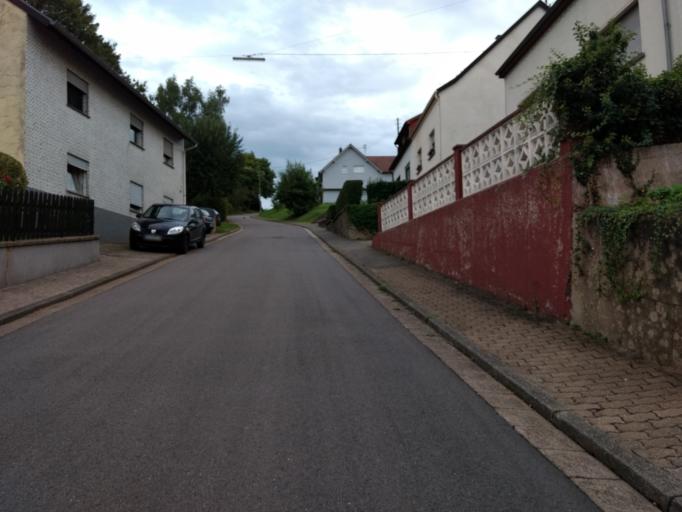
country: DE
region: Saarland
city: Schmelz
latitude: 49.3883
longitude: 6.8413
